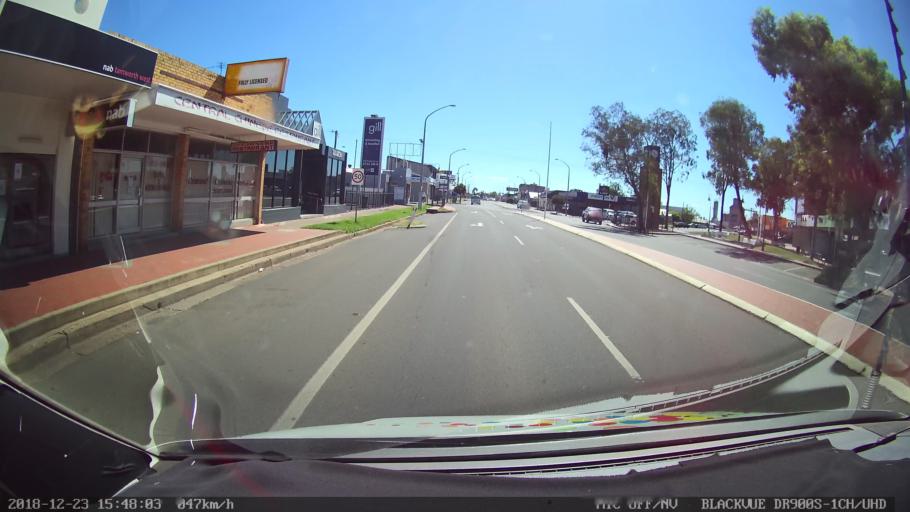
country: AU
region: New South Wales
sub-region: Tamworth Municipality
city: Tamworth
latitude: -31.0940
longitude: 150.9162
